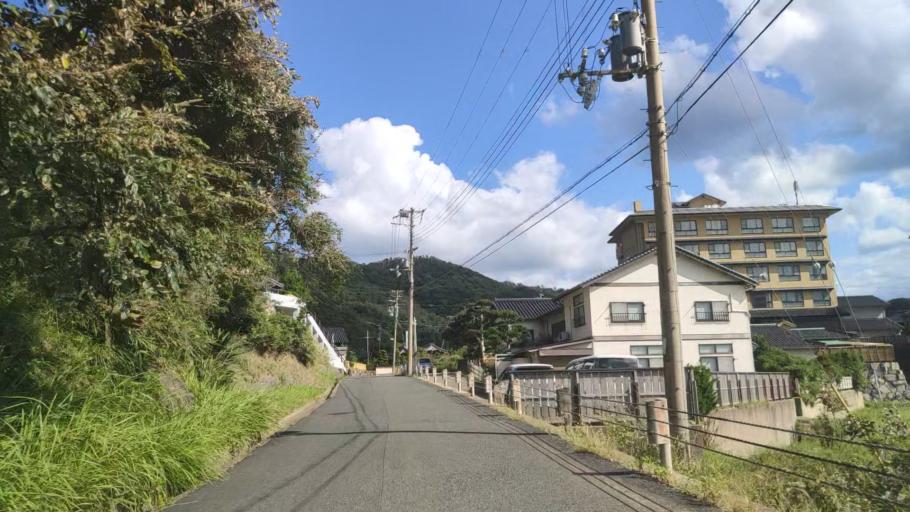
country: JP
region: Hyogo
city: Toyooka
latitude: 35.6694
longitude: 134.9678
